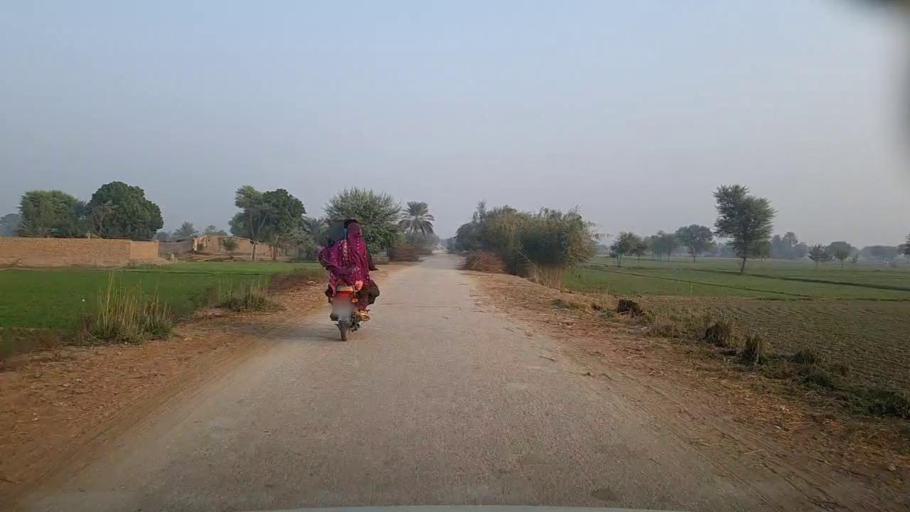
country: PK
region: Sindh
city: Bozdar
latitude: 27.0800
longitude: 68.5748
